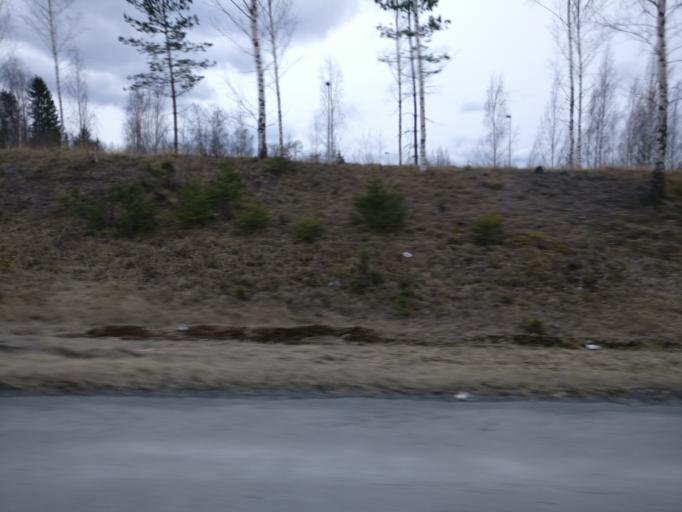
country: FI
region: Haeme
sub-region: Haemeenlinna
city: Parola
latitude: 61.0475
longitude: 24.3594
